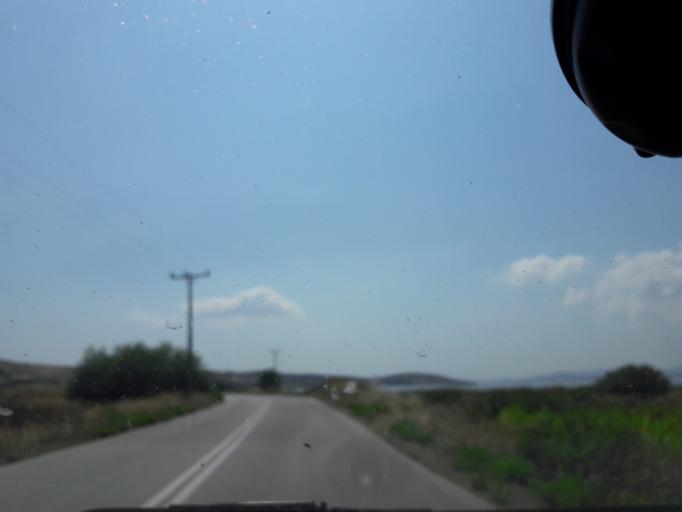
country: GR
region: North Aegean
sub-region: Nomos Lesvou
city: Myrina
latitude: 39.8643
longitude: 25.2661
